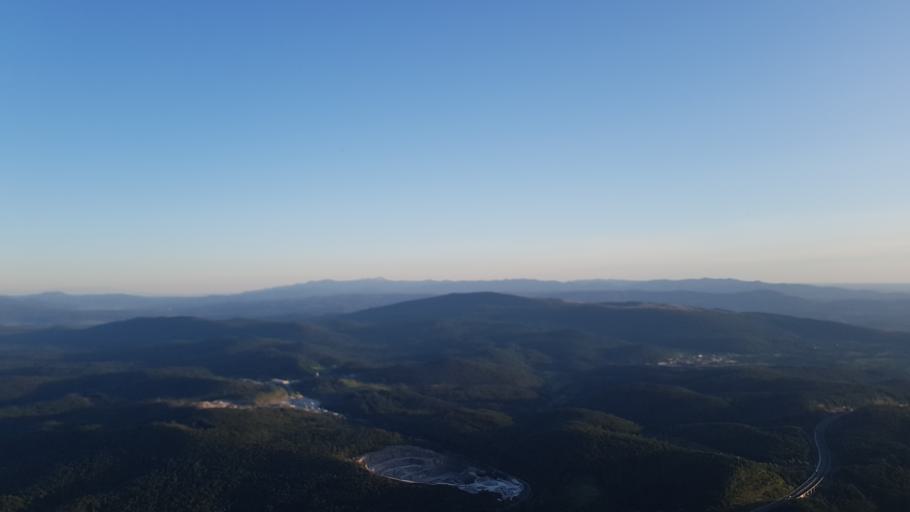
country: SI
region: Vipava
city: Vipava
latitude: 45.7706
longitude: 14.0539
